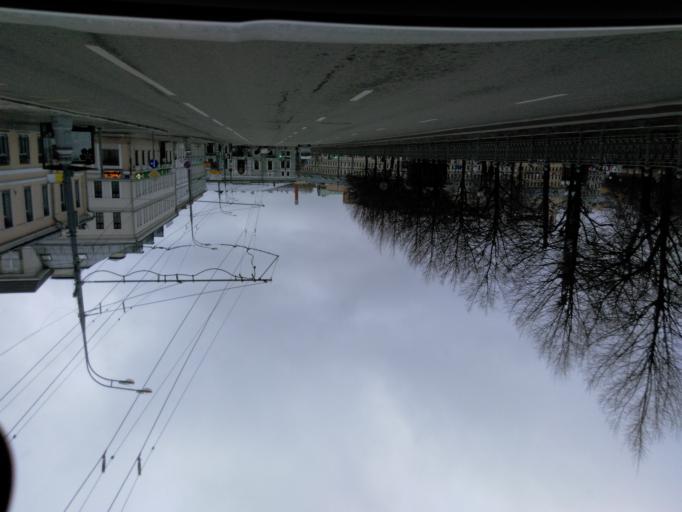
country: RU
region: Moscow
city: Moscow
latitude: 55.7688
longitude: 37.6210
